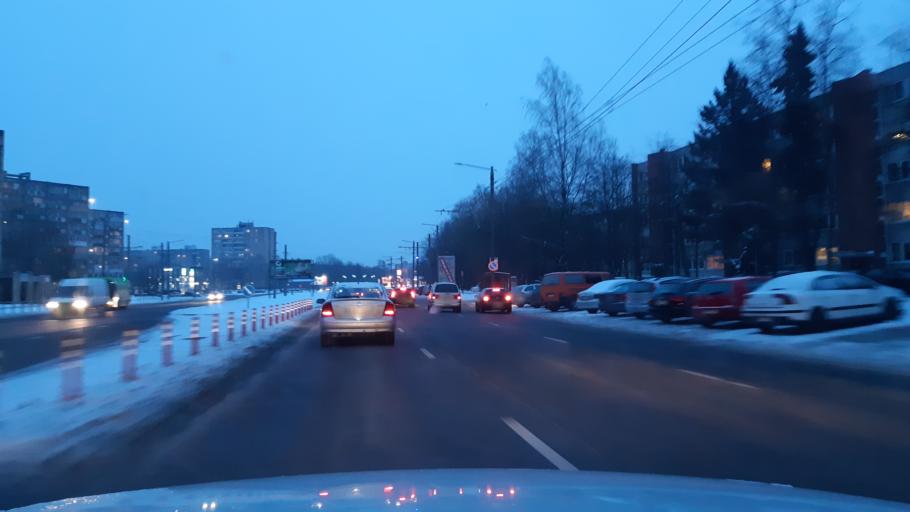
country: LT
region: Kauno apskritis
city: Dainava (Kaunas)
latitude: 54.9118
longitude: 23.9510
